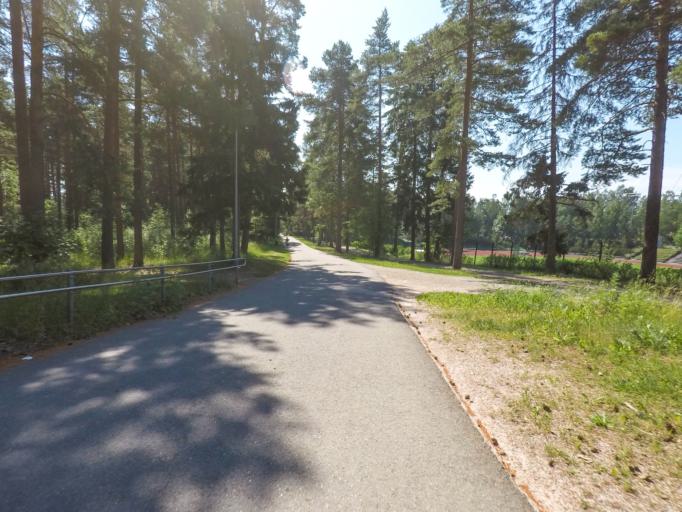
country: FI
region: Uusimaa
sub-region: Helsinki
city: Vantaa
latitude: 60.2177
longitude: 25.1399
